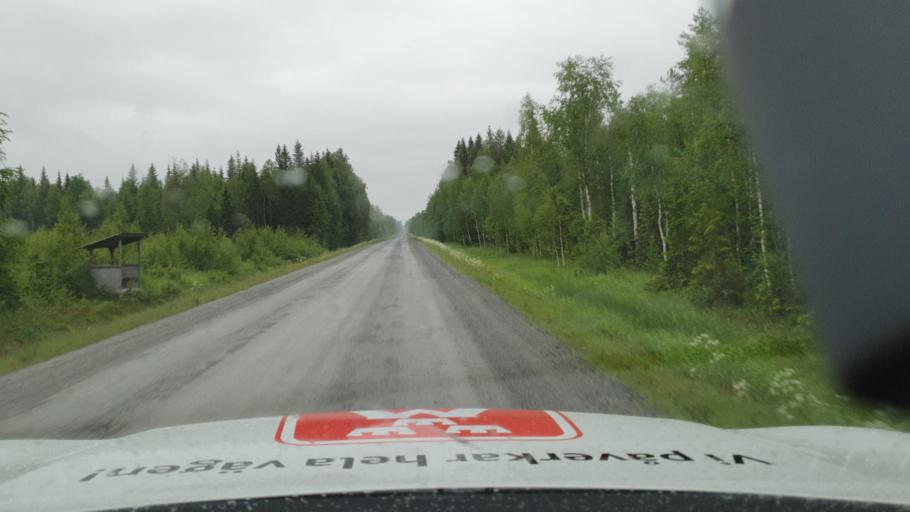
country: SE
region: Vaesterbotten
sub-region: Nordmalings Kommun
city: Nordmaling
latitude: 63.8382
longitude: 19.4838
